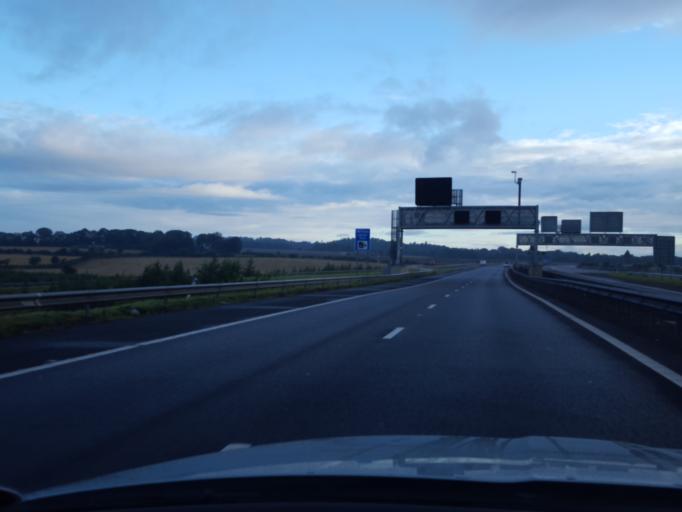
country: GB
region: Scotland
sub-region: Edinburgh
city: Kirkliston
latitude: 55.9558
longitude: -3.4185
